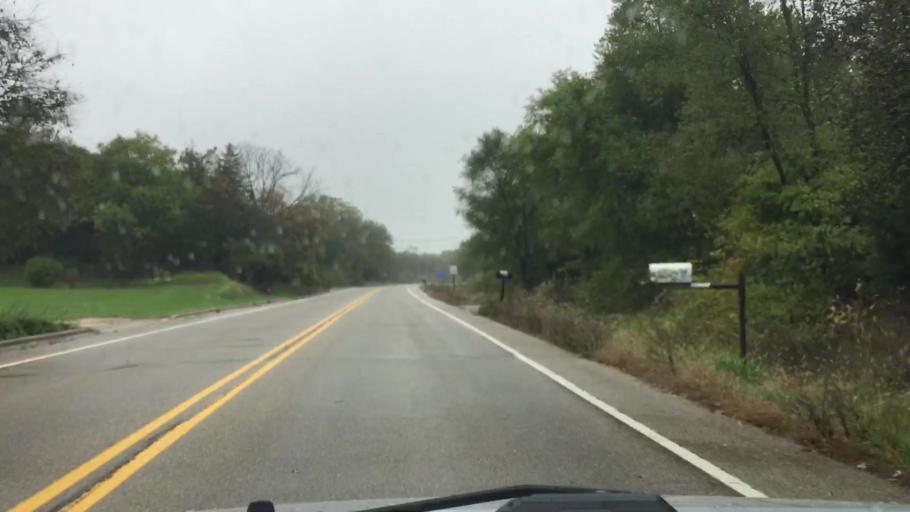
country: US
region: Wisconsin
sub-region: Waukesha County
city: Eagle
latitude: 42.8790
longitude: -88.4800
